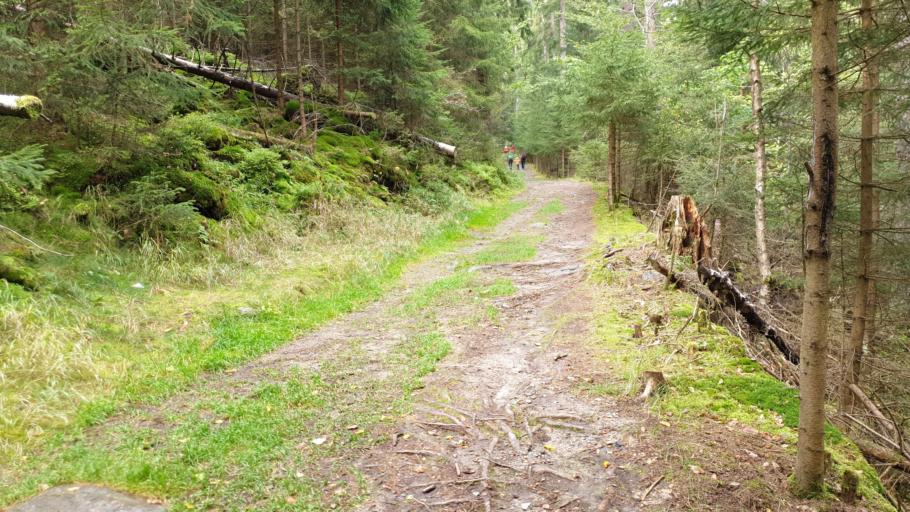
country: DE
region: Saxony
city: Pobershau
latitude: 50.6288
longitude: 13.2380
